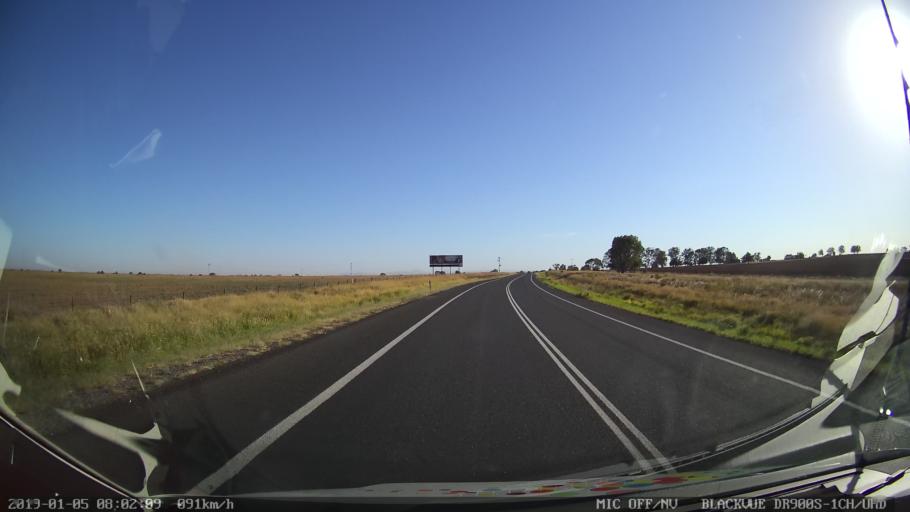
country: AU
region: New South Wales
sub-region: Gilgandra
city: Gilgandra
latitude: -31.6787
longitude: 148.7084
